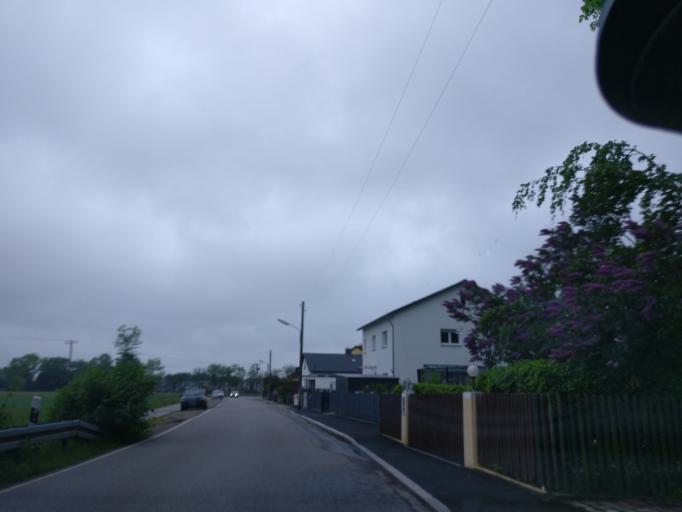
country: DE
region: Bavaria
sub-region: Upper Bavaria
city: Grobenzell
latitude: 48.1817
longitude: 11.4082
